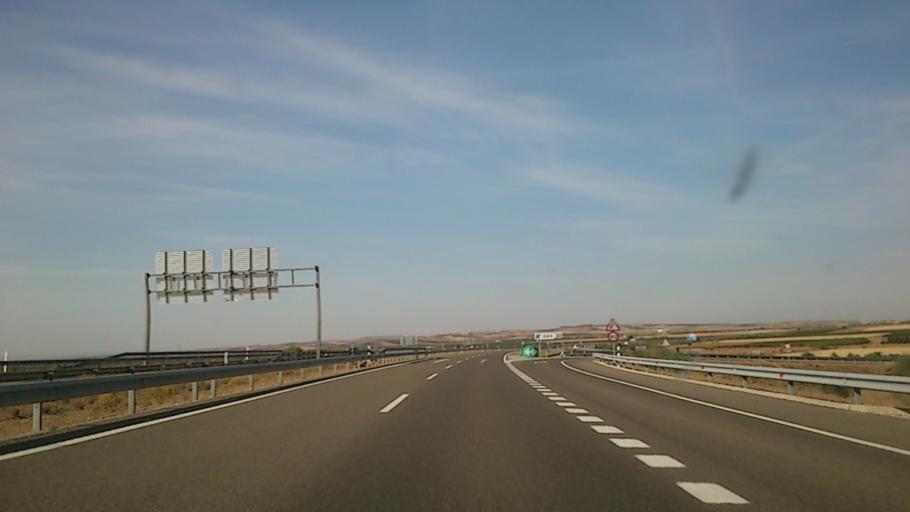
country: ES
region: Aragon
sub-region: Provincia de Zaragoza
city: Carinena
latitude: 41.3681
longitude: -1.2029
